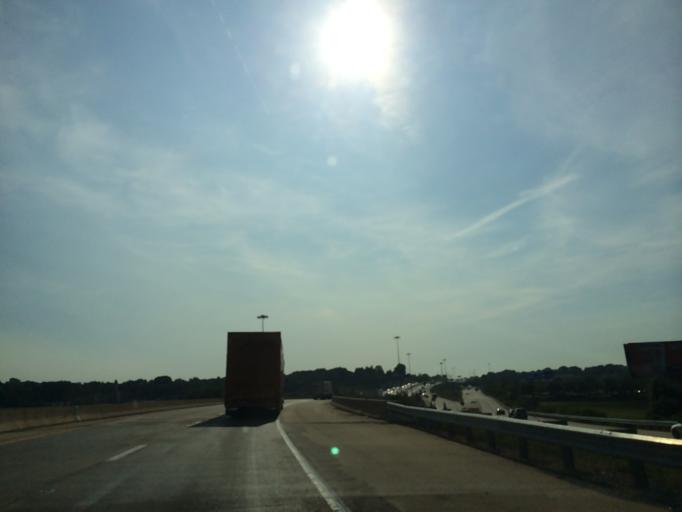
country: US
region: Pennsylvania
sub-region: Lancaster County
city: Lancaster
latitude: 40.0708
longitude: -76.3256
